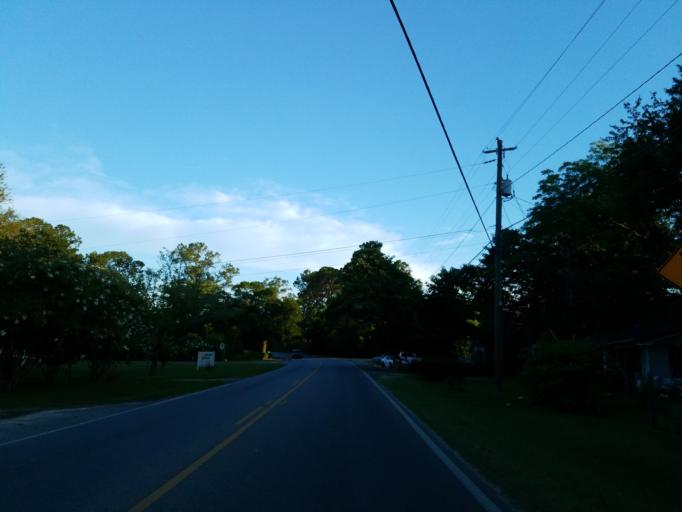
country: US
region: Georgia
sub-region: Cook County
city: Sparks
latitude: 31.1609
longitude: -83.4368
